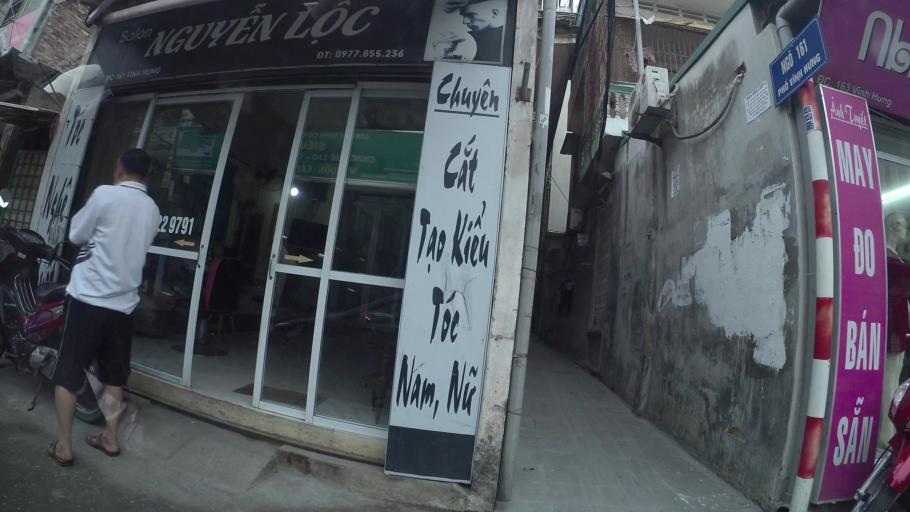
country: VN
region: Ha Noi
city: Hai BaTrung
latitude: 20.9875
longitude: 105.8770
